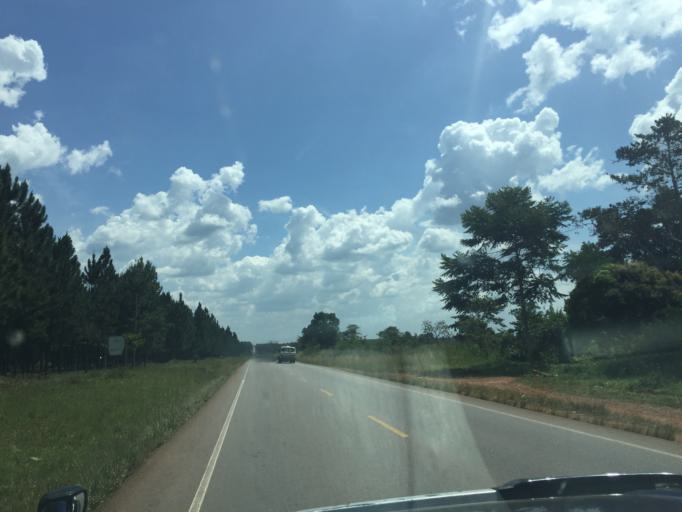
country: UG
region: Central Region
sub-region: Nakasongola District
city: Nakasongola
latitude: 1.2179
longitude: 32.4652
